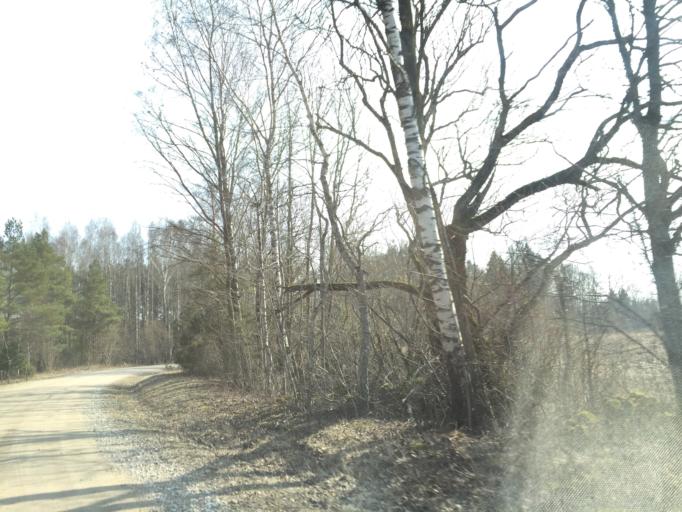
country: EE
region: Saare
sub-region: Kuressaare linn
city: Kuressaare
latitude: 58.3829
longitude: 22.7063
